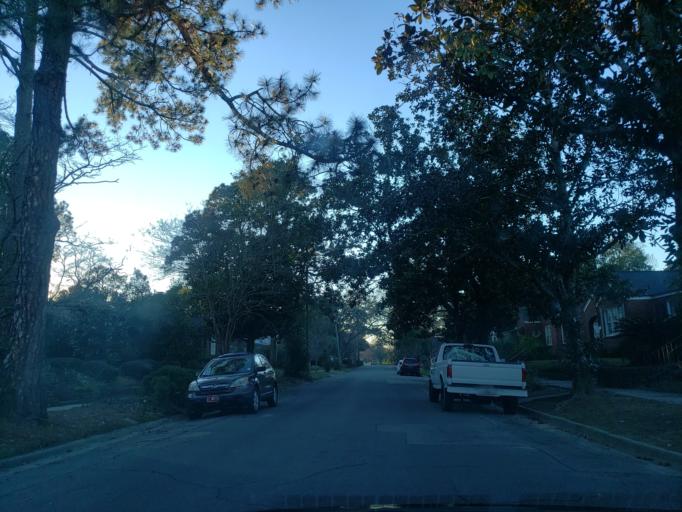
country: US
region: Georgia
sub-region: Chatham County
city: Thunderbolt
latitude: 32.0397
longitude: -81.0907
